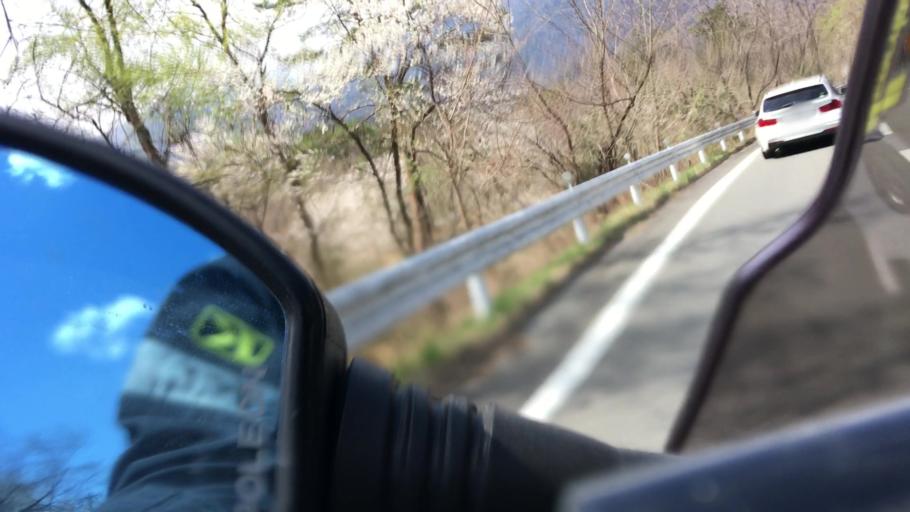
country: JP
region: Yamanashi
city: Nirasaki
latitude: 35.7791
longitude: 138.3279
